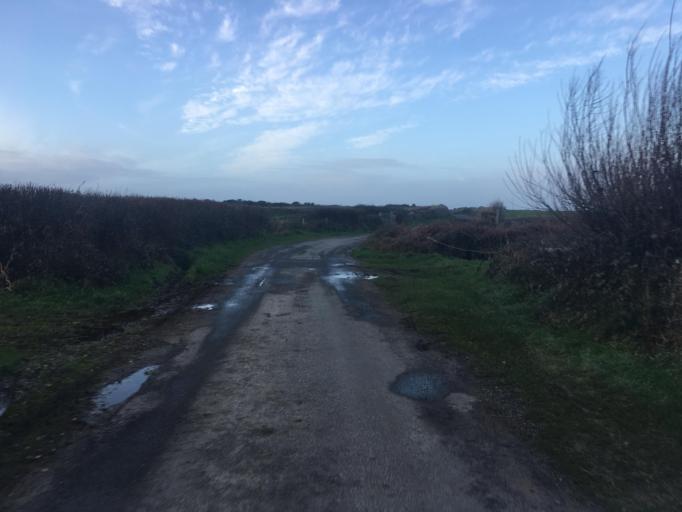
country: FR
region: Lower Normandy
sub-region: Departement de la Manche
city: Beaumont-Hague
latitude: 49.7206
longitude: -1.9211
